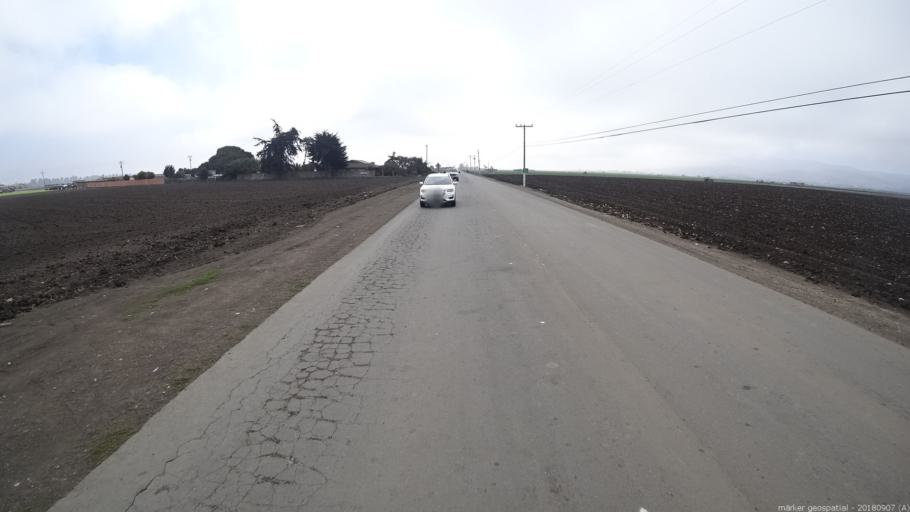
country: US
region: California
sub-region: Monterey County
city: Salinas
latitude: 36.6567
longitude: -121.6880
